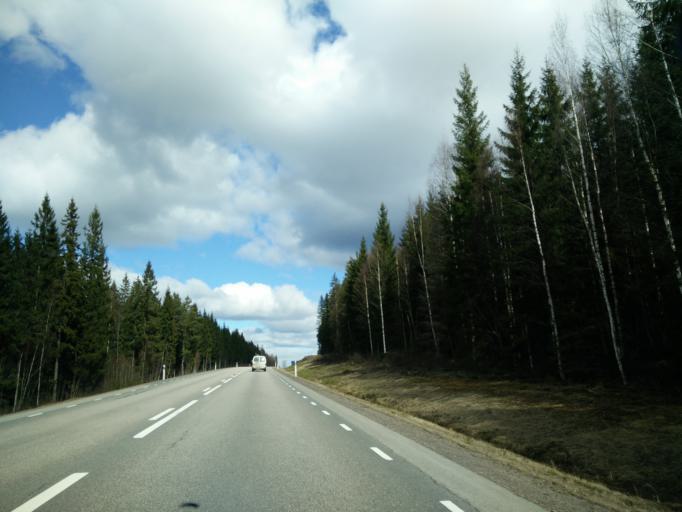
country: SE
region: Vaermland
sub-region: Hagfors Kommun
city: Hagfors
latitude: 59.9901
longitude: 13.5892
